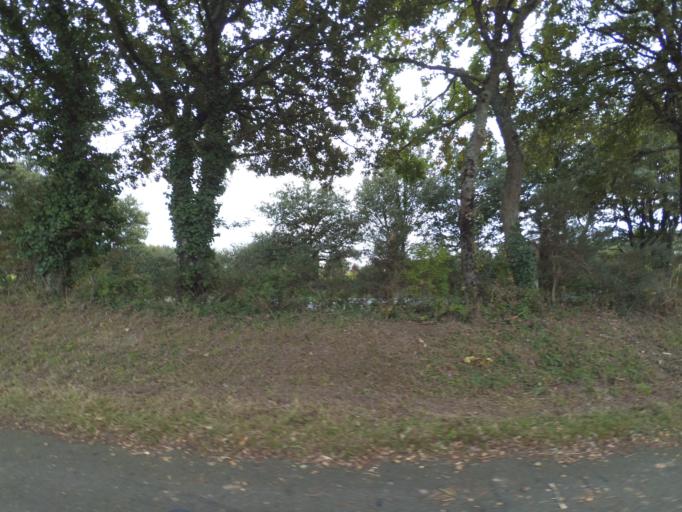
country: FR
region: Pays de la Loire
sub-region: Departement de la Vendee
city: Bouffere
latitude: 46.9742
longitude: -1.3409
